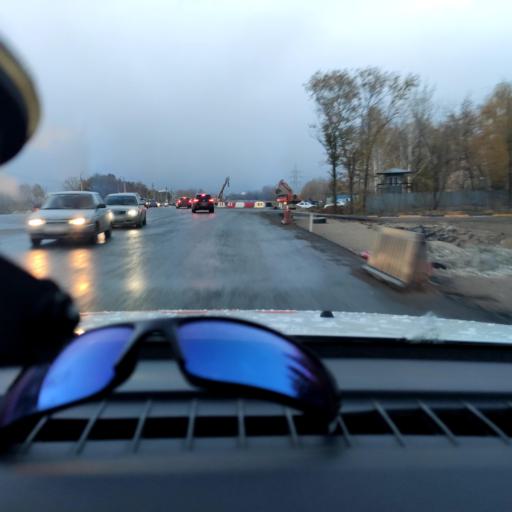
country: RU
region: Samara
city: Samara
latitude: 53.1387
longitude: 50.1026
